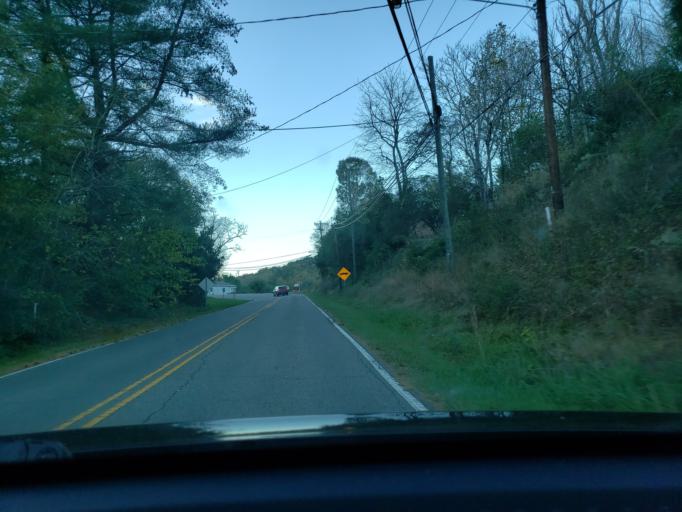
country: US
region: North Carolina
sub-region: Stokes County
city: Danbury
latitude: 36.4083
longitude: -80.2023
